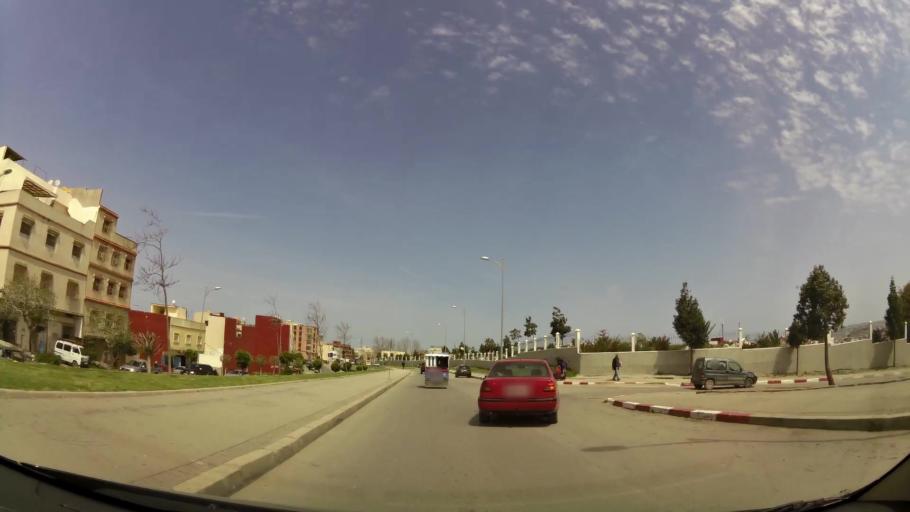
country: MA
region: Tanger-Tetouan
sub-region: Tanger-Assilah
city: Tangier
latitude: 35.7485
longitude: -5.8289
